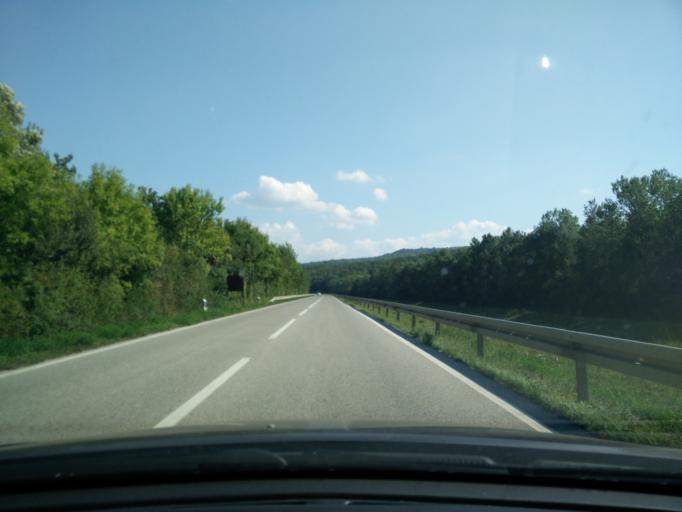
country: HR
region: Istarska
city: Buje
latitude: 45.3563
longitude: 13.7411
